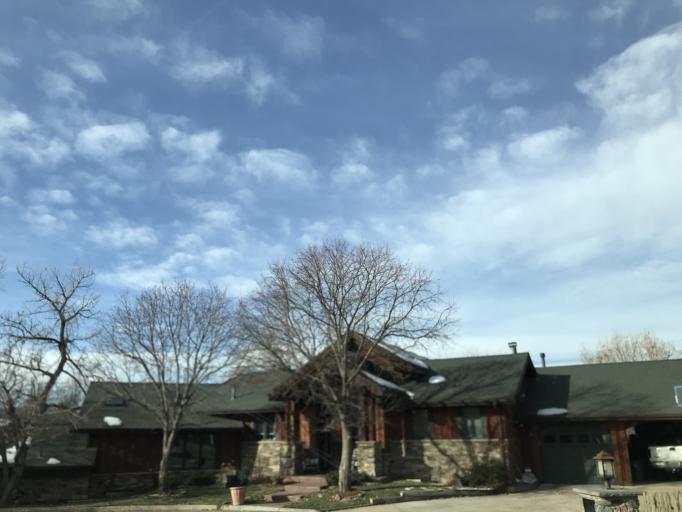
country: US
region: Colorado
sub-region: Arapahoe County
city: Columbine Valley
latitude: 39.5967
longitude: -105.0176
